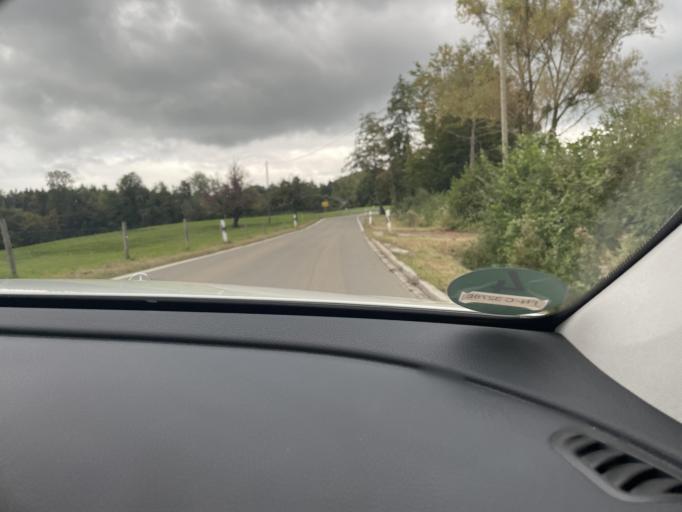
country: DE
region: Baden-Wuerttemberg
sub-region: Tuebingen Region
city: Markdorf
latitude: 47.7289
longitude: 9.3938
